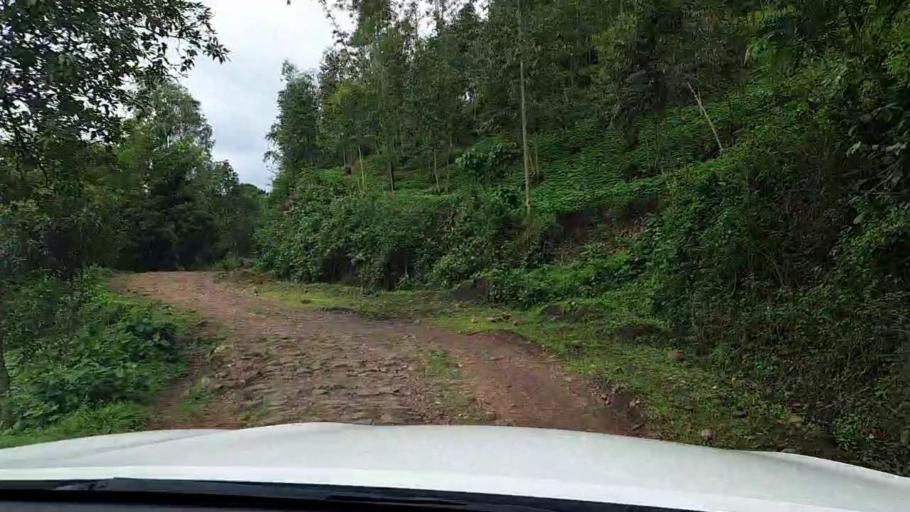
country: RW
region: Western Province
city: Cyangugu
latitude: -2.5566
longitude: 29.0358
